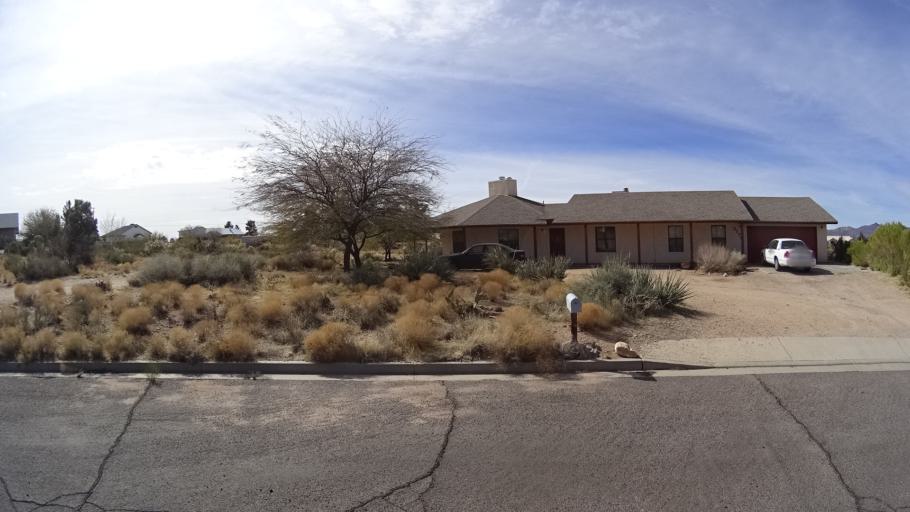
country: US
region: Arizona
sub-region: Mohave County
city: Kingman
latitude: 35.1878
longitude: -113.9910
